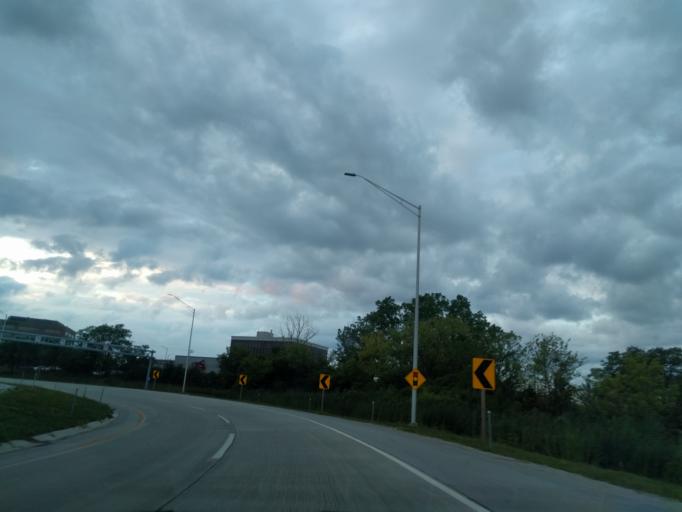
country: US
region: Illinois
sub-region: Cook County
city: Elk Grove Village
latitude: 42.0413
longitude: -87.9814
